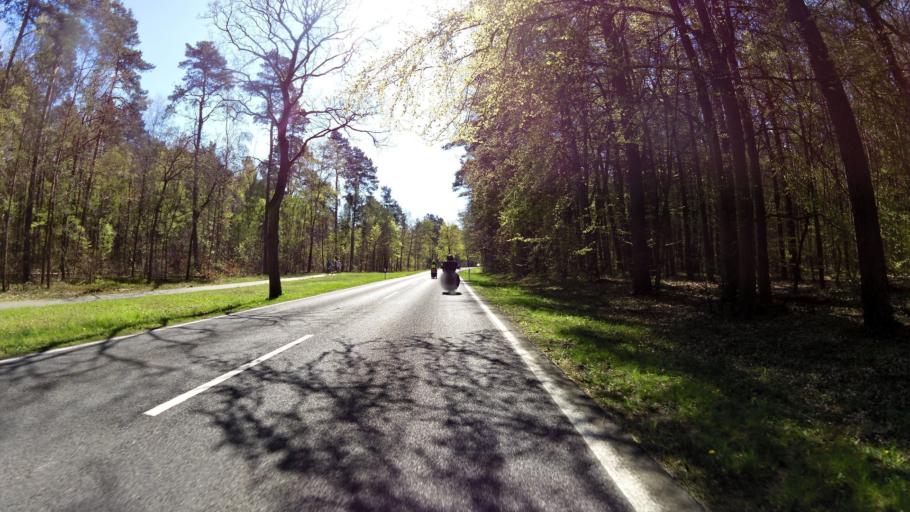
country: DE
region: Brandenburg
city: Bernau bei Berlin
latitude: 52.7129
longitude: 13.5321
